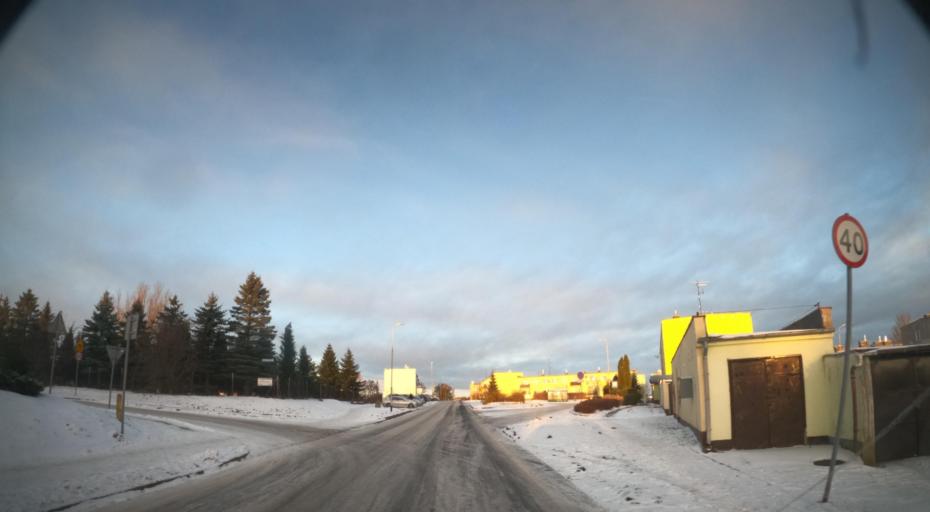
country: PL
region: West Pomeranian Voivodeship
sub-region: Powiat koszalinski
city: Sianow
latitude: 54.2321
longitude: 16.3071
